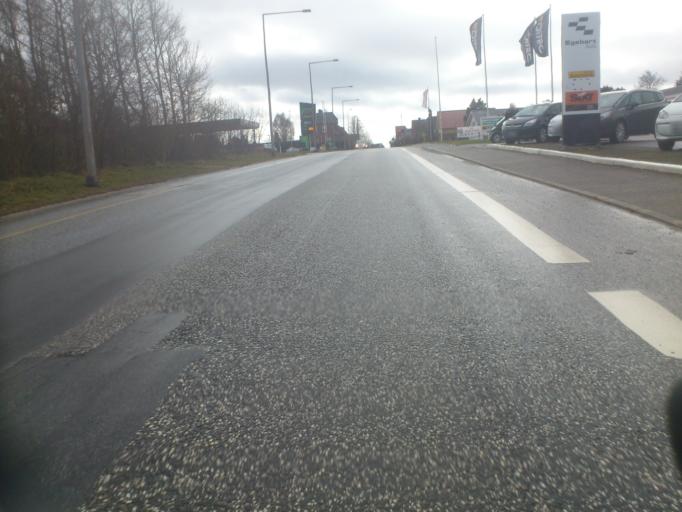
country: DK
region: South Denmark
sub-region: Fredericia Kommune
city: Fredericia
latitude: 55.5817
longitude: 9.7538
